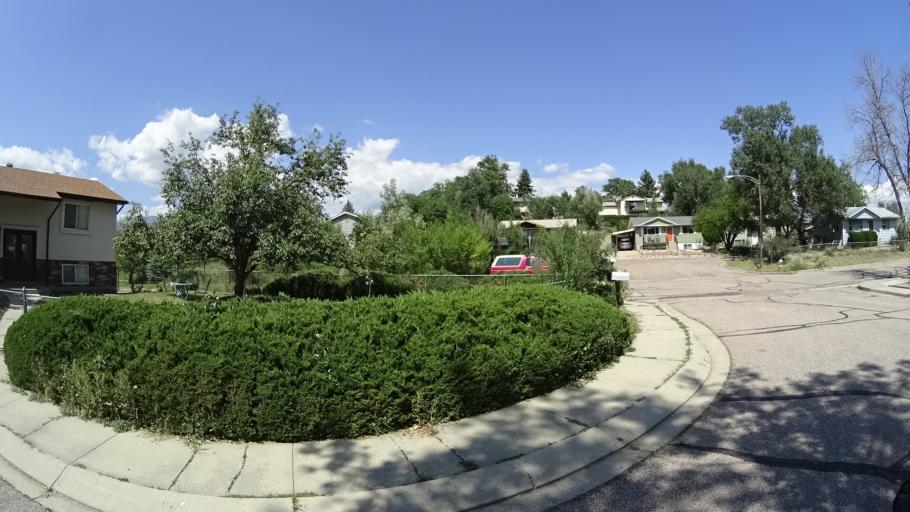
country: US
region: Colorado
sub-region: El Paso County
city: Colorado Springs
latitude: 38.8628
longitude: -104.8395
